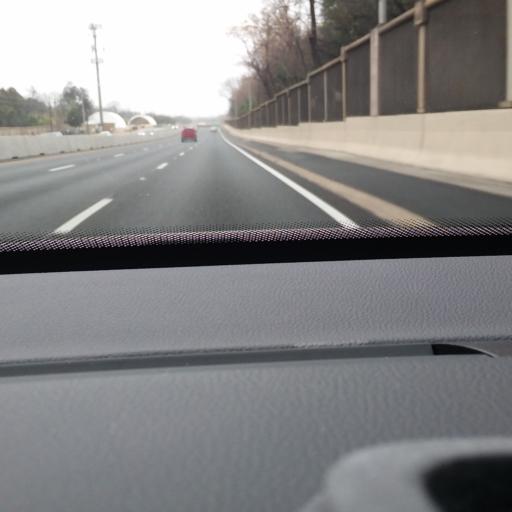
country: US
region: Texas
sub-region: Dallas County
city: Highland Park
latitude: 32.8387
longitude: -96.7836
